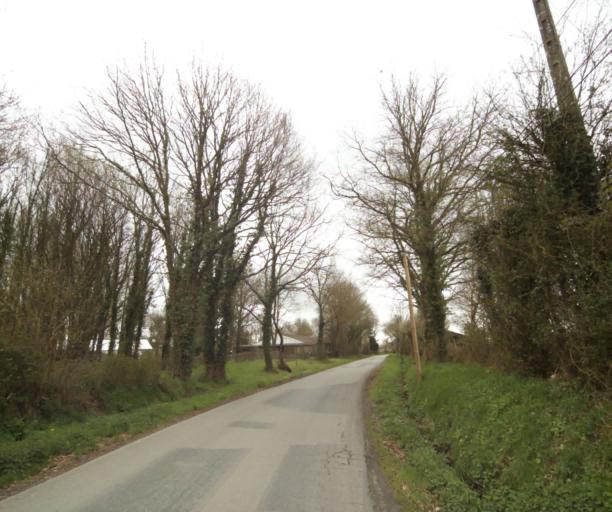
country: FR
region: Pays de la Loire
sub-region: Departement de la Loire-Atlantique
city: Bouvron
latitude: 47.4332
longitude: -1.8578
